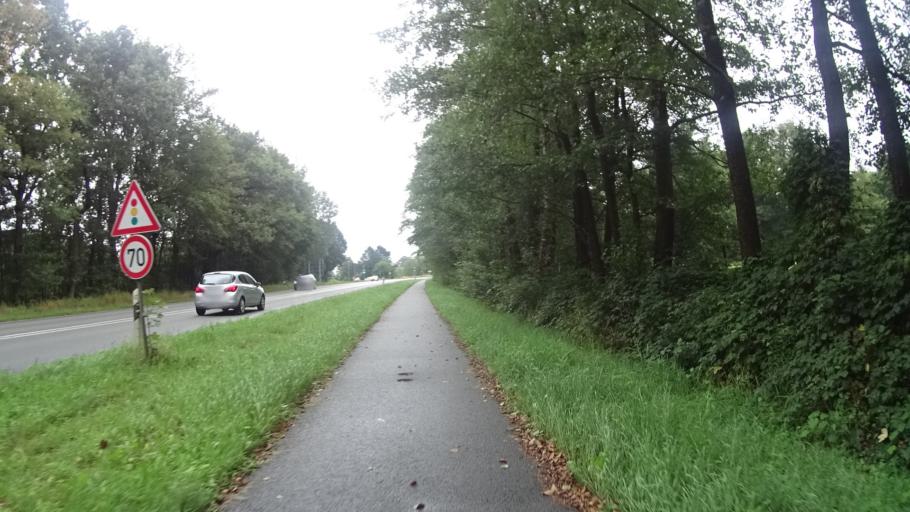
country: DE
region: Lower Saxony
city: Brinkum
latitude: 53.2656
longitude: 7.5467
